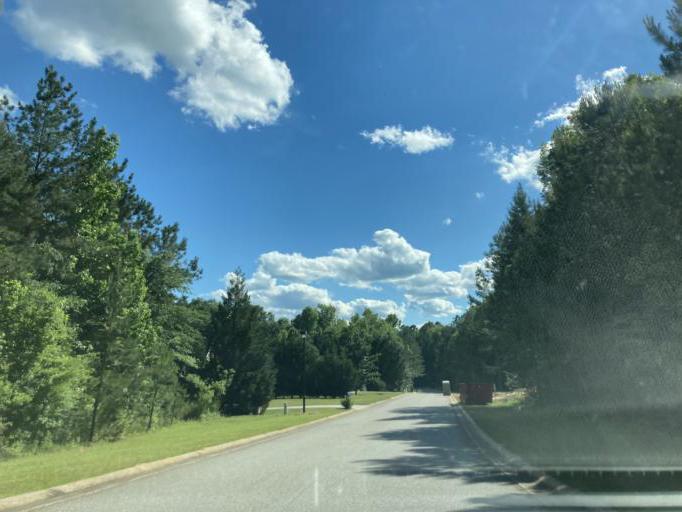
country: US
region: Georgia
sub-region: Jones County
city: Gray
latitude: 33.0008
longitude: -83.5465
